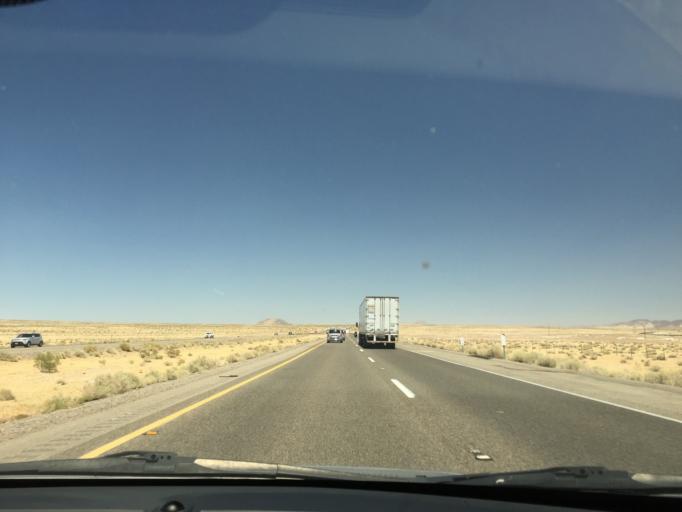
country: US
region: California
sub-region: San Bernardino County
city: Fort Irwin
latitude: 34.9946
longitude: -116.5736
